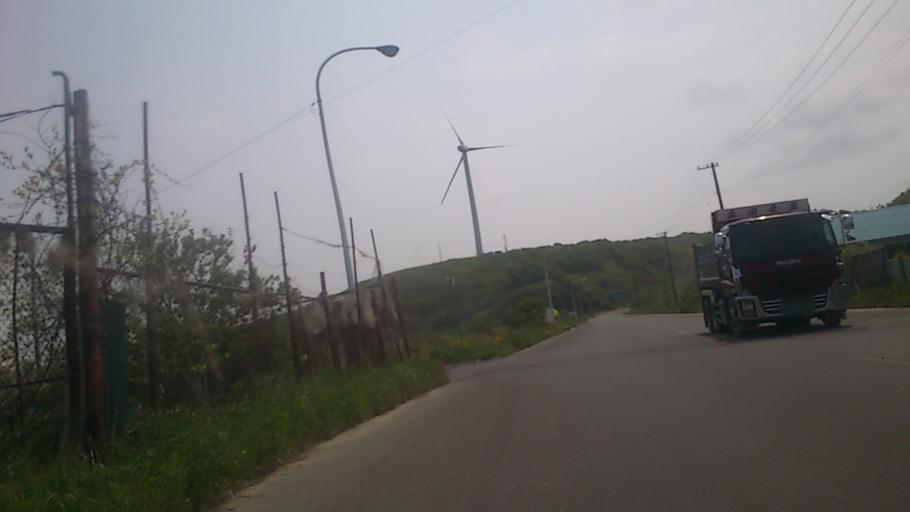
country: JP
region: Hokkaido
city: Nemuro
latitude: 43.2809
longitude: 145.5639
